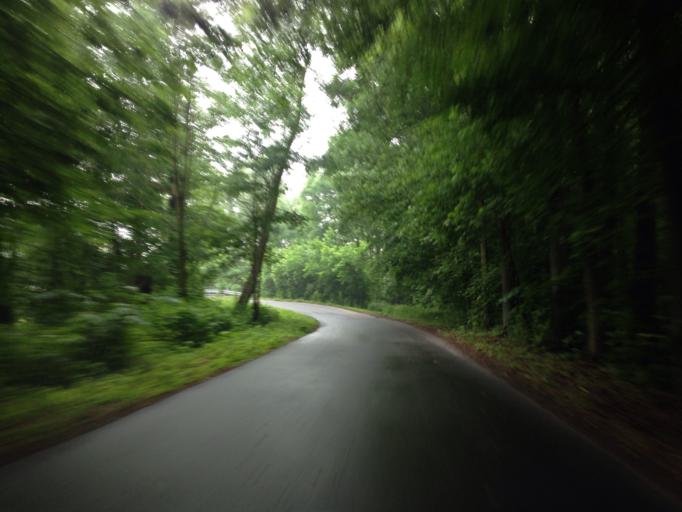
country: PL
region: Kujawsko-Pomorskie
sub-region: Powiat brodnicki
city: Jablonowo Pomorskie
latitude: 53.4451
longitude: 19.1892
